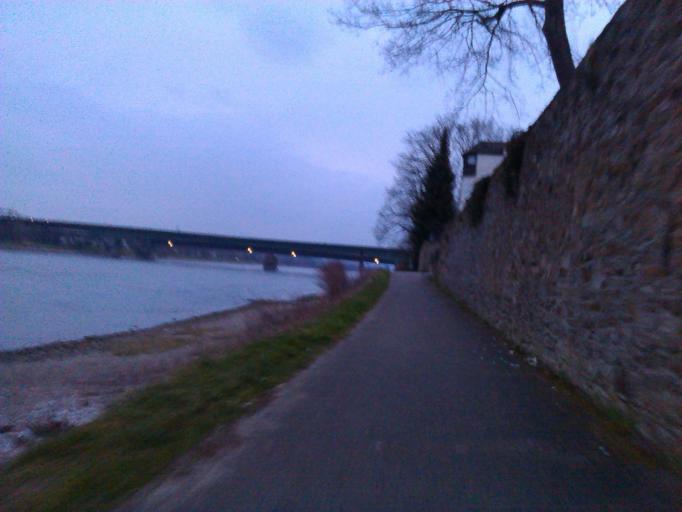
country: DE
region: Rheinland-Pfalz
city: Koblenz
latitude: 50.3277
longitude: 7.5937
